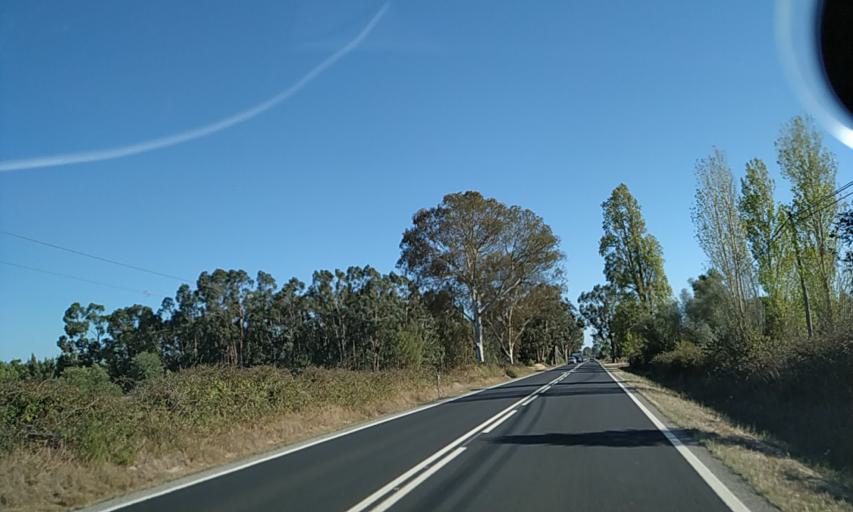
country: PT
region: Santarem
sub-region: Benavente
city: Poceirao
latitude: 38.8041
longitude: -8.8808
